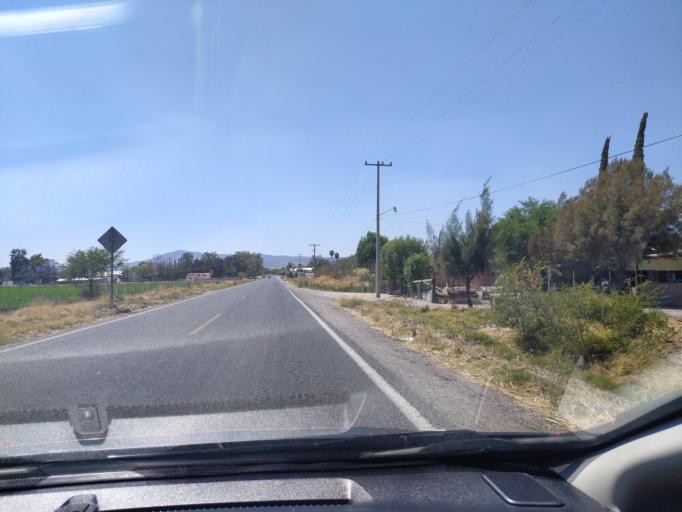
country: MX
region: Guanajuato
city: Ciudad Manuel Doblado
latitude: 20.7451
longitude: -101.9006
